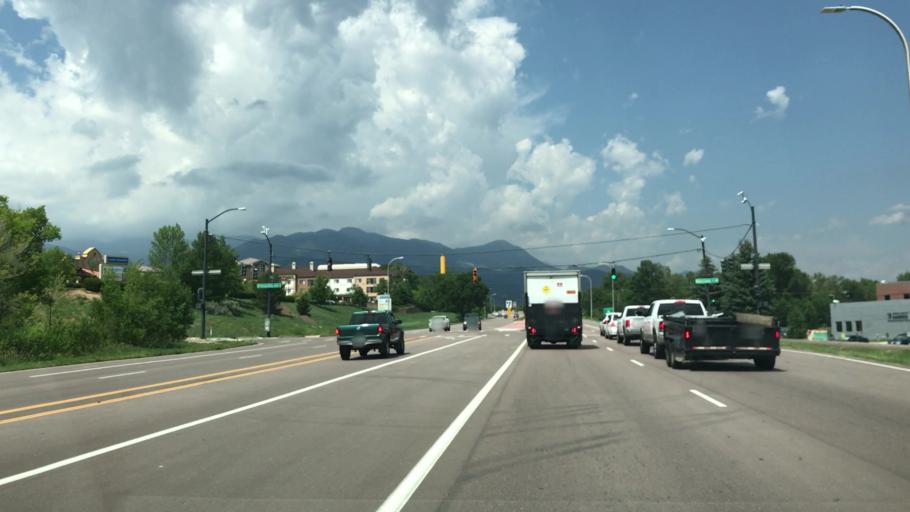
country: US
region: Colorado
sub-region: El Paso County
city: Stratmoor
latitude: 38.7963
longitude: -104.8103
